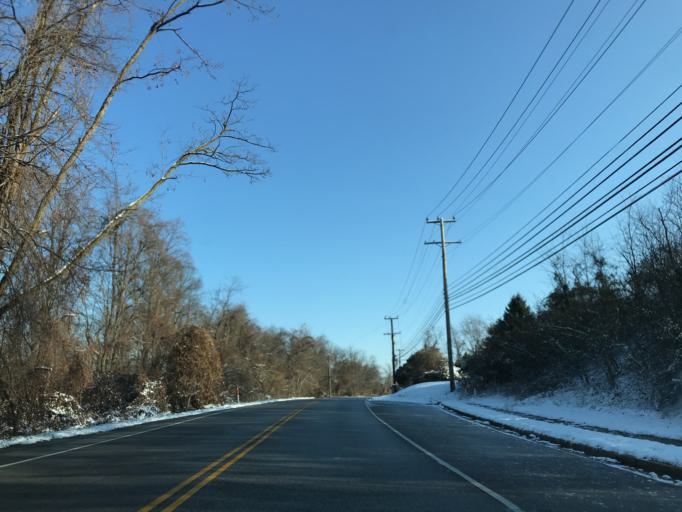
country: US
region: Maryland
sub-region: Anne Arundel County
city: Linthicum
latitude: 39.2217
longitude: -76.6741
